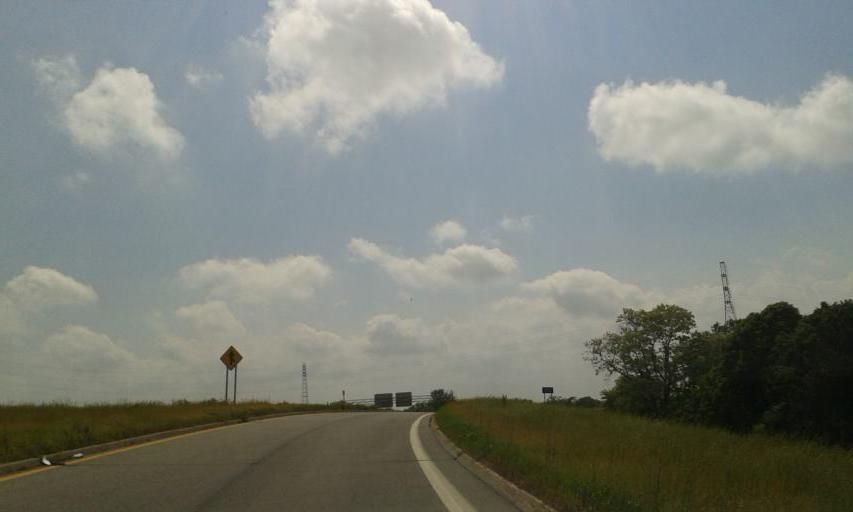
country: US
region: New York
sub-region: Niagara County
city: Niagara Falls
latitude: 43.0751
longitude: -78.9939
